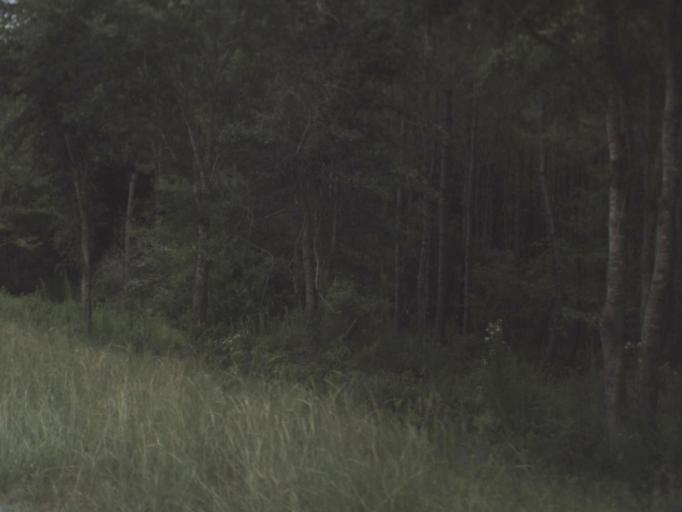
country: US
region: Florida
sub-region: Union County
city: Lake Butler
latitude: 29.9238
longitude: -82.4094
